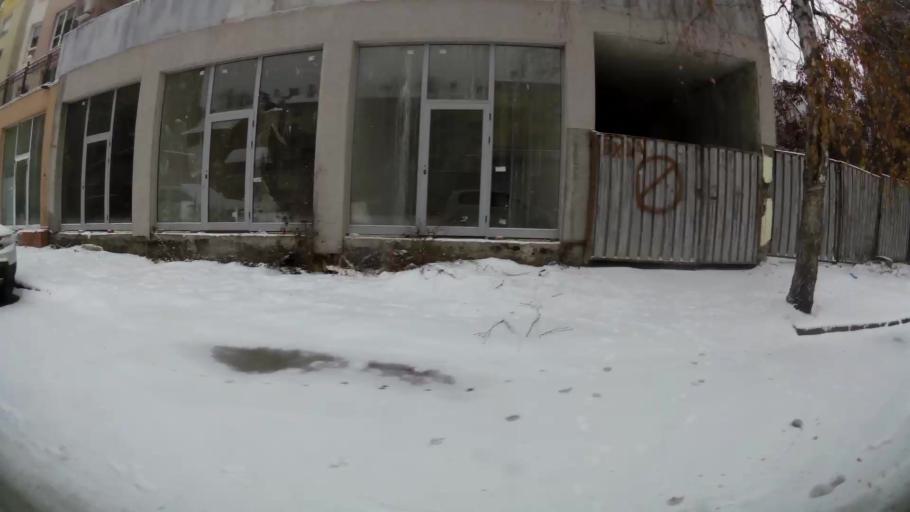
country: BG
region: Sofia-Capital
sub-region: Stolichna Obshtina
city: Sofia
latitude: 42.7008
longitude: 23.2994
